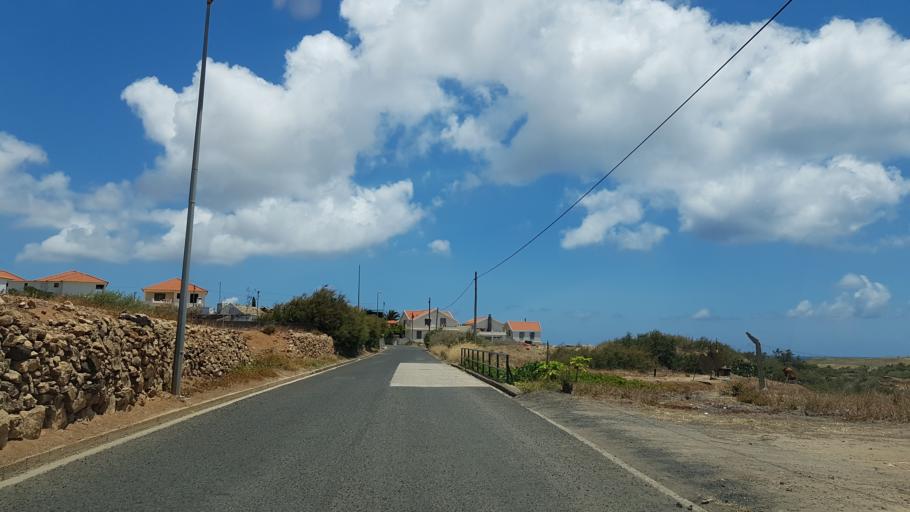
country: PT
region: Madeira
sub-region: Porto Santo
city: Vila de Porto Santo
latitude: 33.0538
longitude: -16.3681
